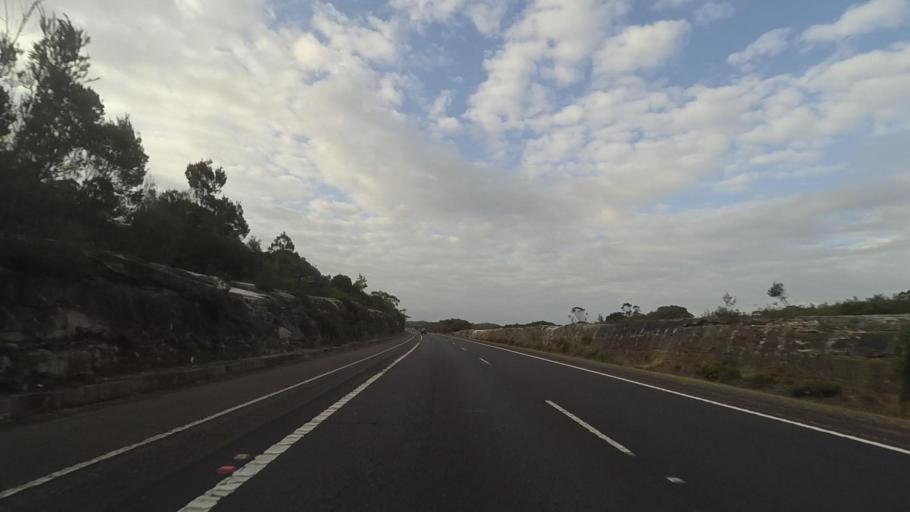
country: AU
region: New South Wales
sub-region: Wollongong
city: Bulli
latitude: -34.2793
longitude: 150.9282
